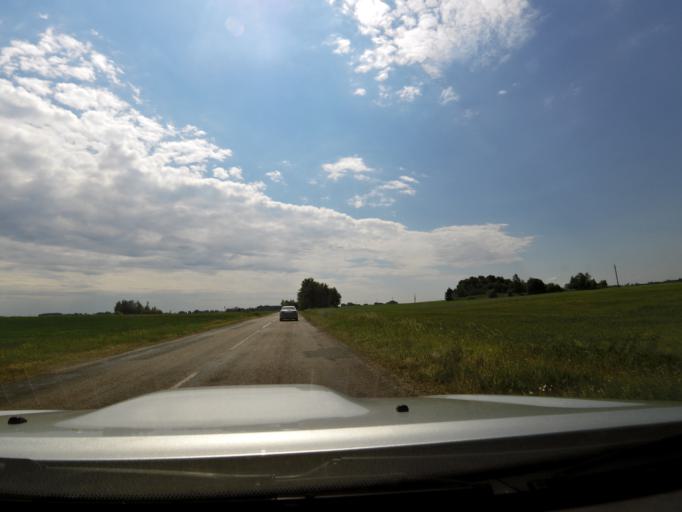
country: LT
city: Vilkaviskis
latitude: 54.5913
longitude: 23.0306
